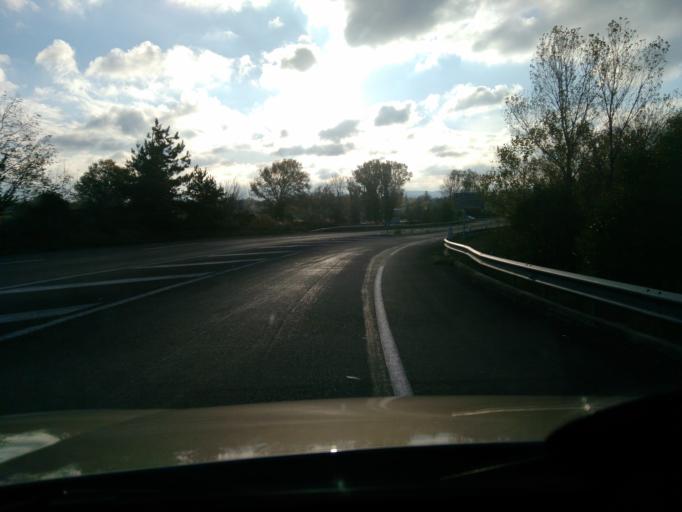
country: FR
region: Rhone-Alpes
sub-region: Departement de la Drome
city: Saint-Marcel-les-Sauzet
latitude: 44.5943
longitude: 4.8004
